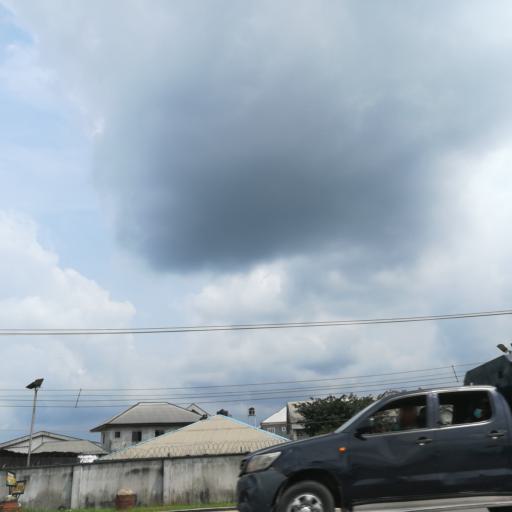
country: NG
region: Rivers
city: Port Harcourt
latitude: 4.8482
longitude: 7.0742
